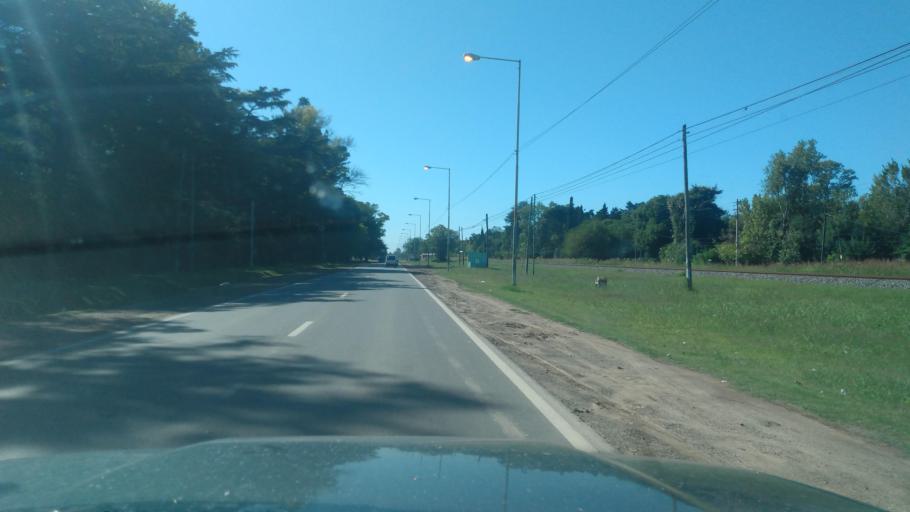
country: AR
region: Buenos Aires
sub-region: Partido de General Rodriguez
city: General Rodriguez
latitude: -34.6027
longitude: -58.9786
